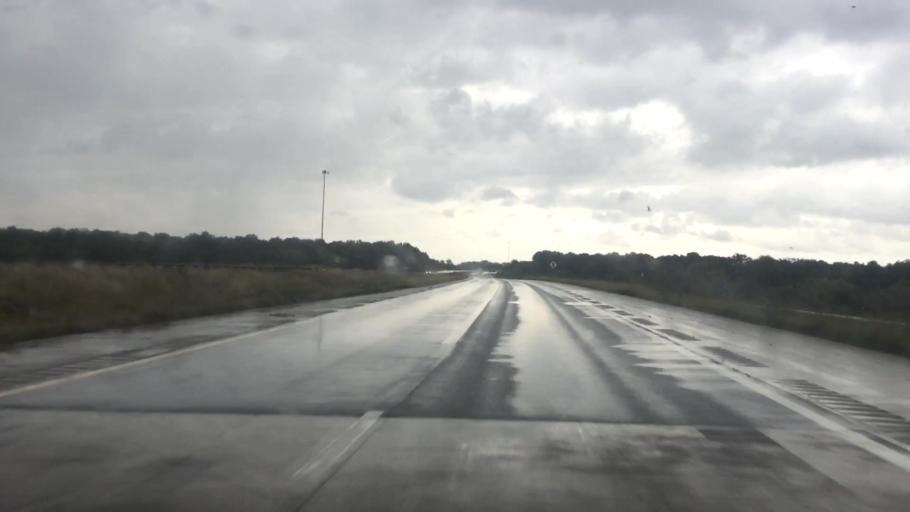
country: US
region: Kansas
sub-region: Miami County
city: Osawatomie
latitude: 38.5002
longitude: -94.9343
